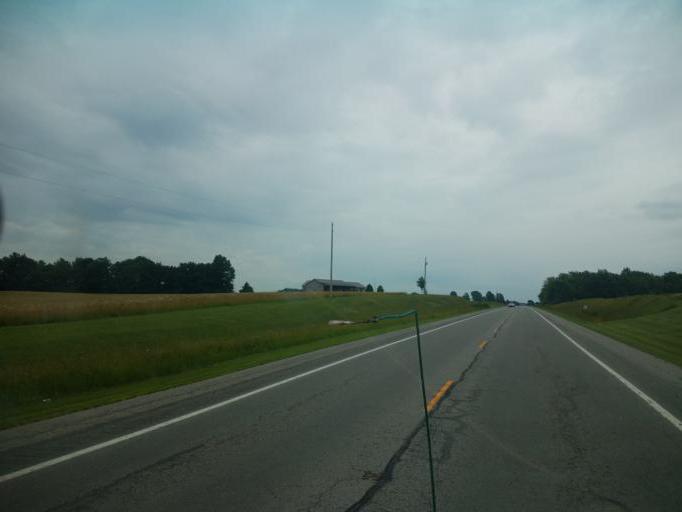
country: US
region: Ohio
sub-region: Hardin County
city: Ada
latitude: 40.7063
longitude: -83.7382
